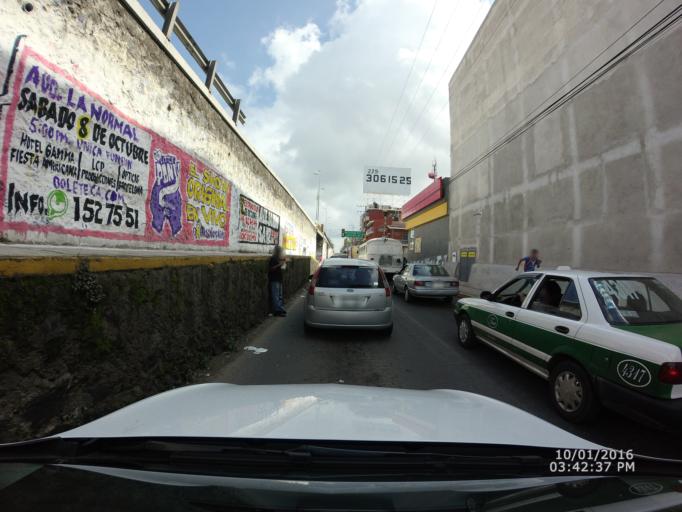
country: MX
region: Veracruz
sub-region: Xalapa
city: Xalapa de Enriquez
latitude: 19.5514
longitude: -96.9131
